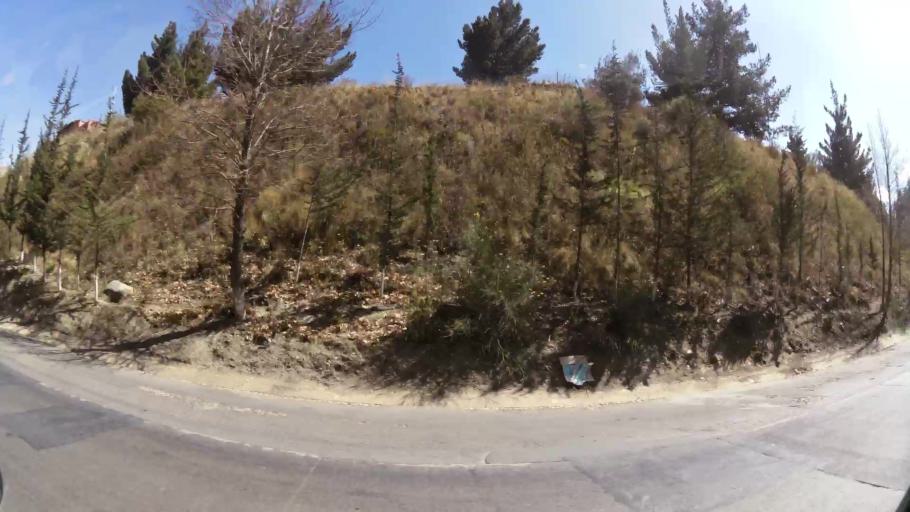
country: BO
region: La Paz
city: La Paz
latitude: -16.4616
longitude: -68.1470
